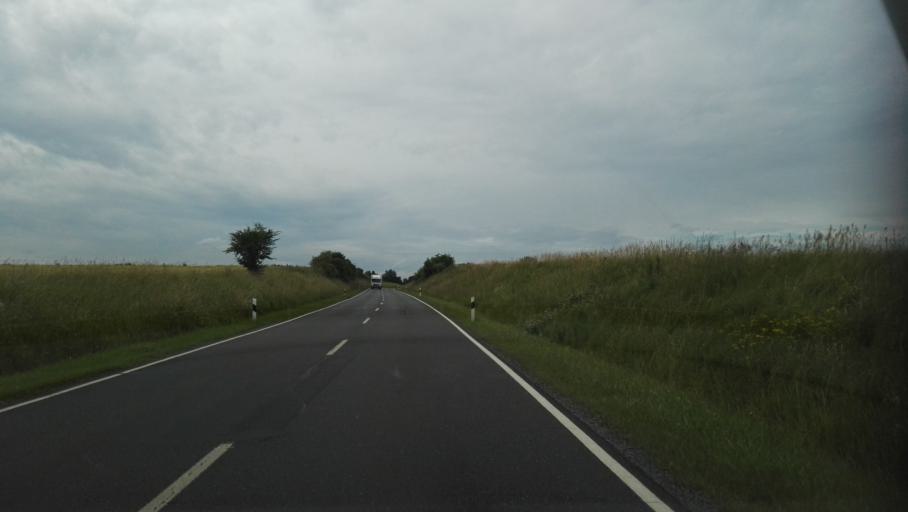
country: DE
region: Bavaria
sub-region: Upper Franconia
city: Hollfeld
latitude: 49.9195
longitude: 11.3090
